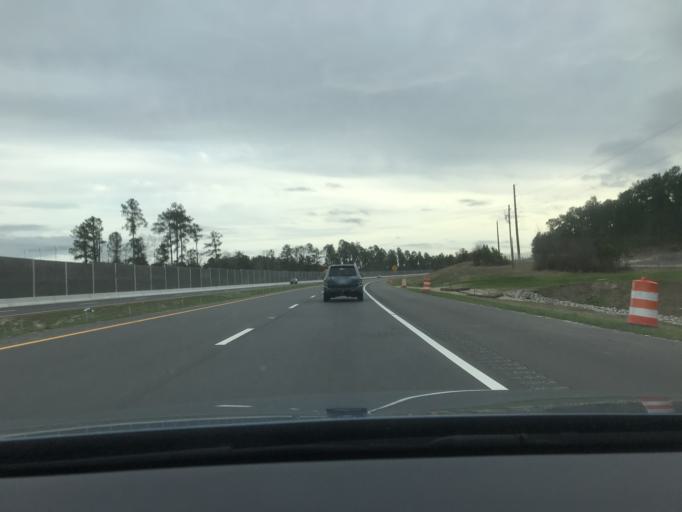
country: US
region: North Carolina
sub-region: Cumberland County
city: Fort Bragg
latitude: 35.0785
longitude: -79.0208
